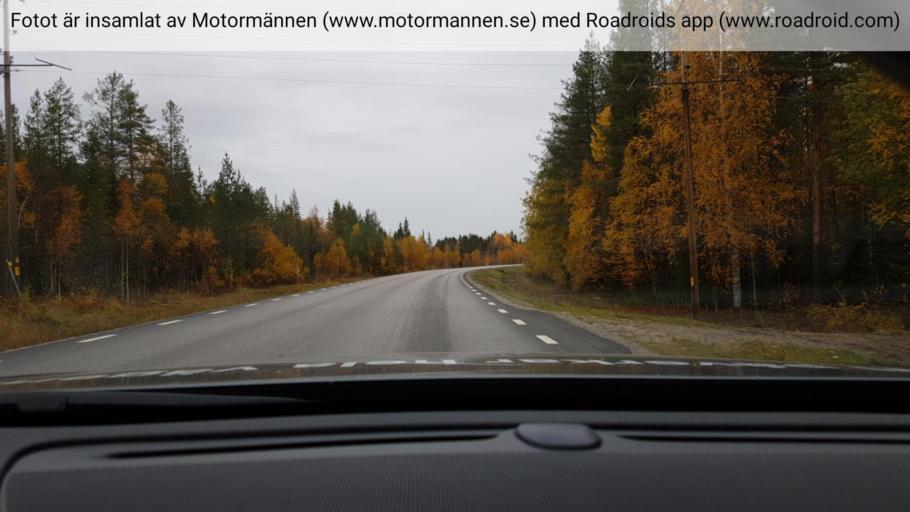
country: SE
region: Norrbotten
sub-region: Overkalix Kommun
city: OEverkalix
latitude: 66.3506
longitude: 22.8263
